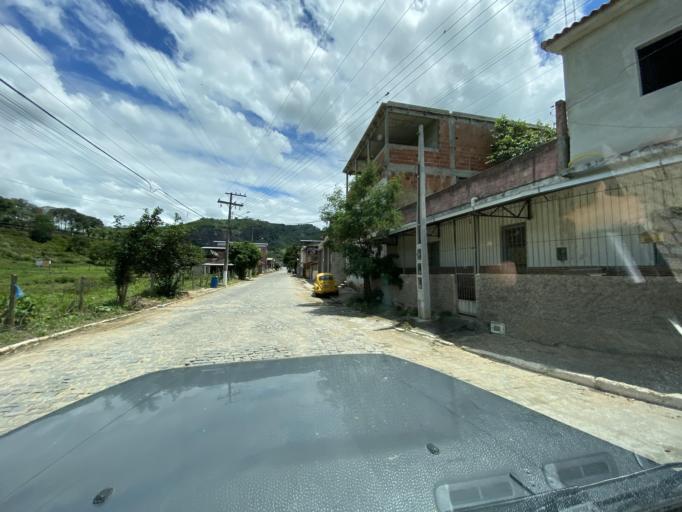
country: BR
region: Espirito Santo
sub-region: Jeronimo Monteiro
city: Jeronimo Monteiro
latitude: -20.7845
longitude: -41.3897
